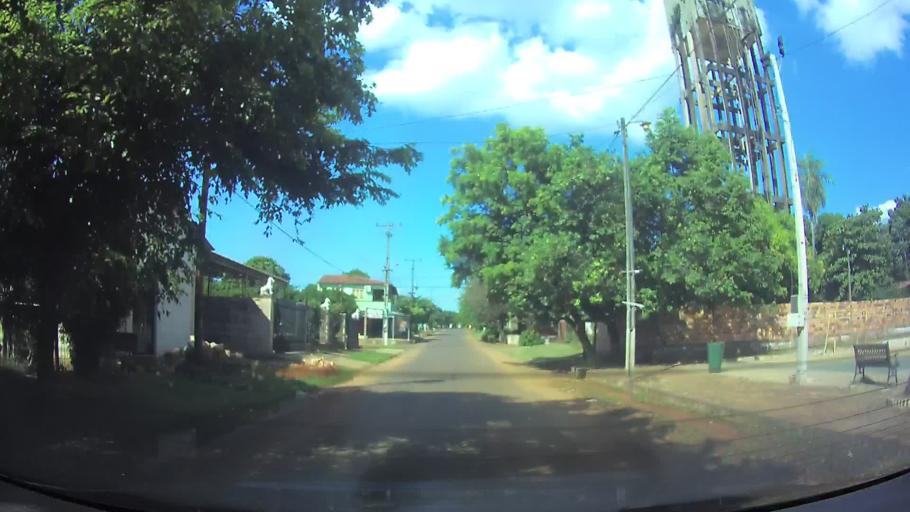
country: PY
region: Central
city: Itaugua
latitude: -25.3890
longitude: -57.3490
